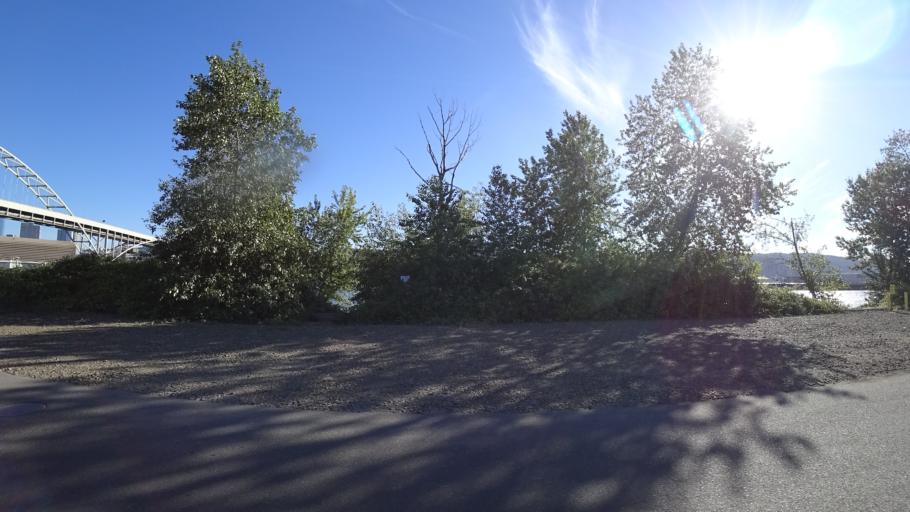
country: US
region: Oregon
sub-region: Multnomah County
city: Portland
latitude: 45.5417
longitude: -122.6843
